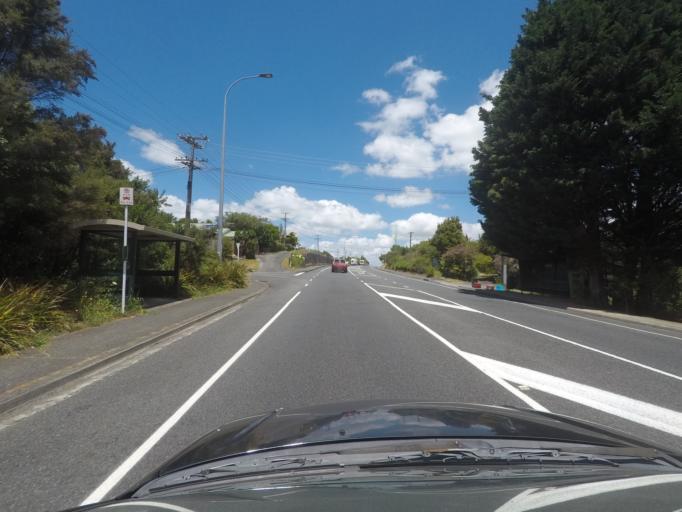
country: NZ
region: Northland
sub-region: Whangarei
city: Whangarei
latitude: -35.7458
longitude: 174.3670
